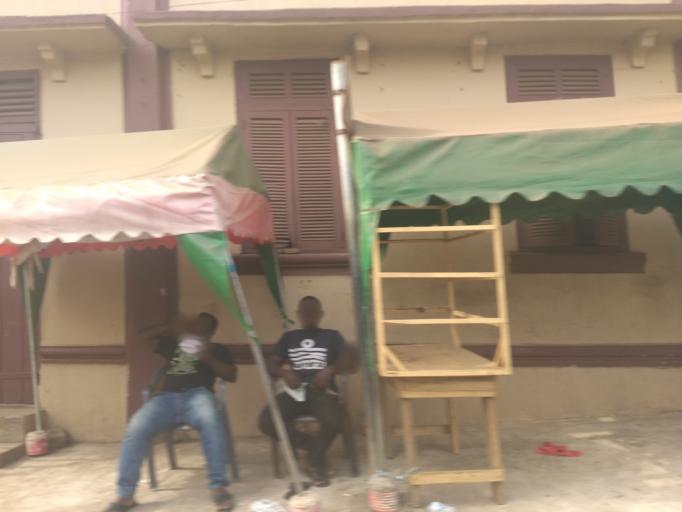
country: GH
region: Ashanti
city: Kumasi
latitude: 6.7023
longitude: -1.6322
